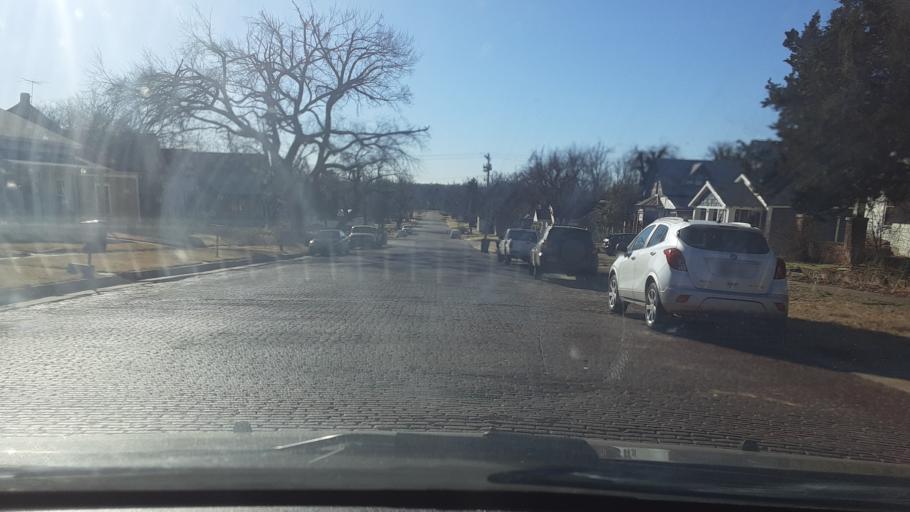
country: US
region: Oklahoma
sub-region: Logan County
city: Guthrie
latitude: 35.8757
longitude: -97.4276
